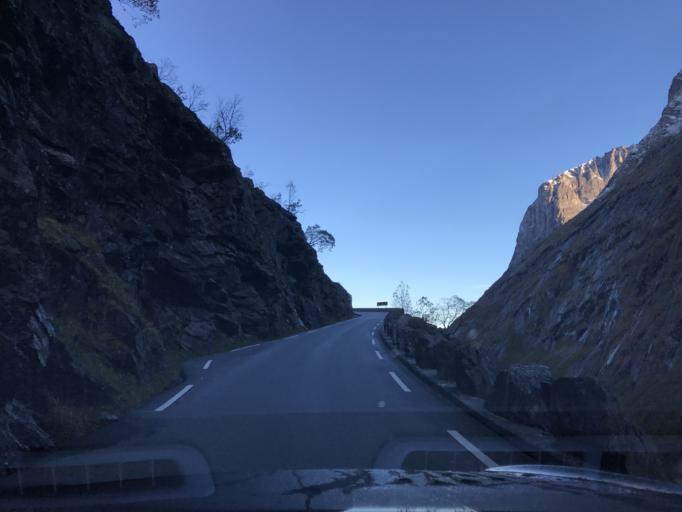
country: NO
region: More og Romsdal
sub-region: Rauma
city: Andalsnes
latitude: 62.4573
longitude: 7.6729
